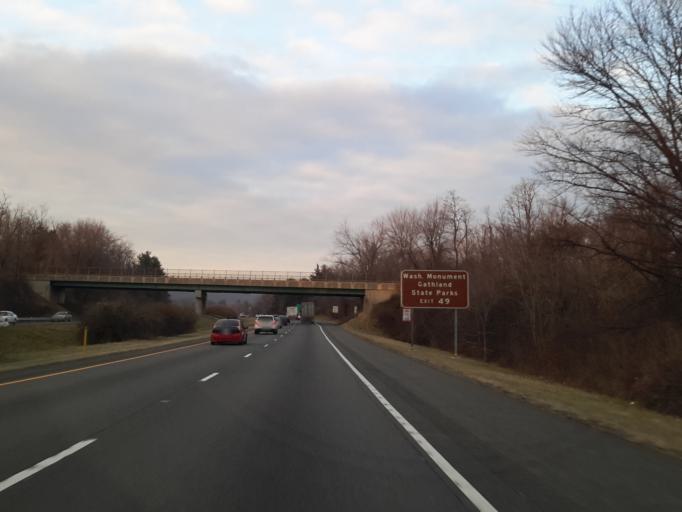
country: US
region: Maryland
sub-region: Frederick County
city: Braddock Heights
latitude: 39.4115
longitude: -77.4732
